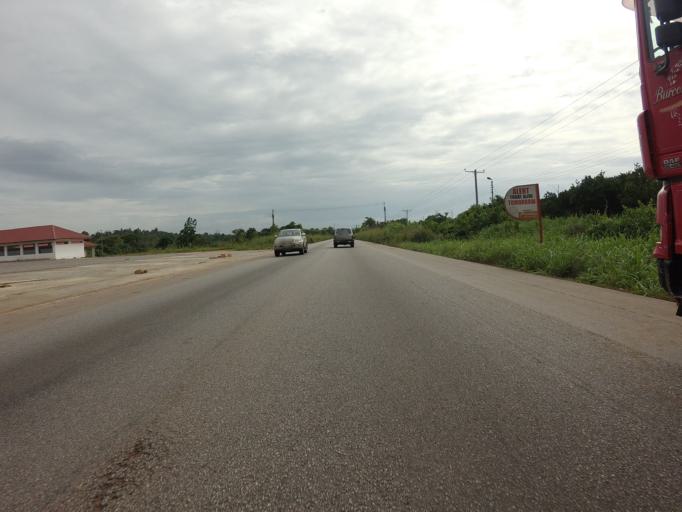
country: GH
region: Eastern
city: Nkawkaw
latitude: 6.6013
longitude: -0.8763
